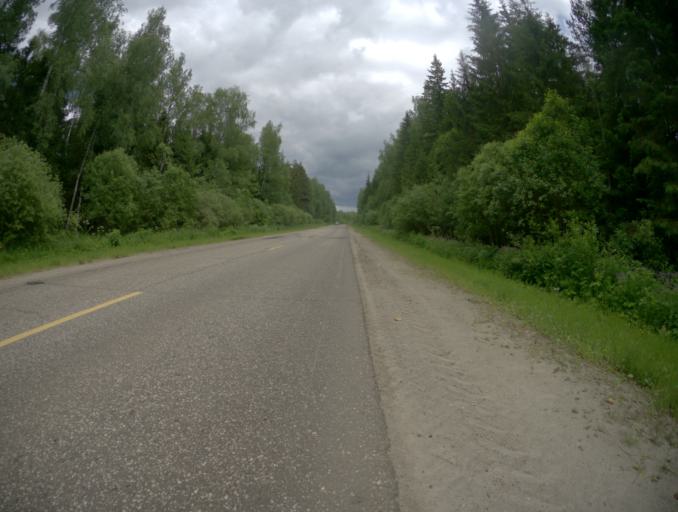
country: RU
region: Ivanovo
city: Arkhipovka
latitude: 56.6190
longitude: 41.2755
